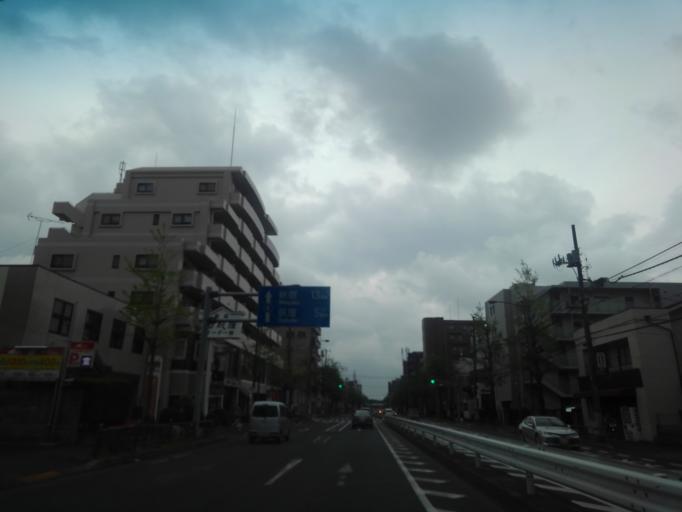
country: JP
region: Tokyo
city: Musashino
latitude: 35.7230
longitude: 139.5745
